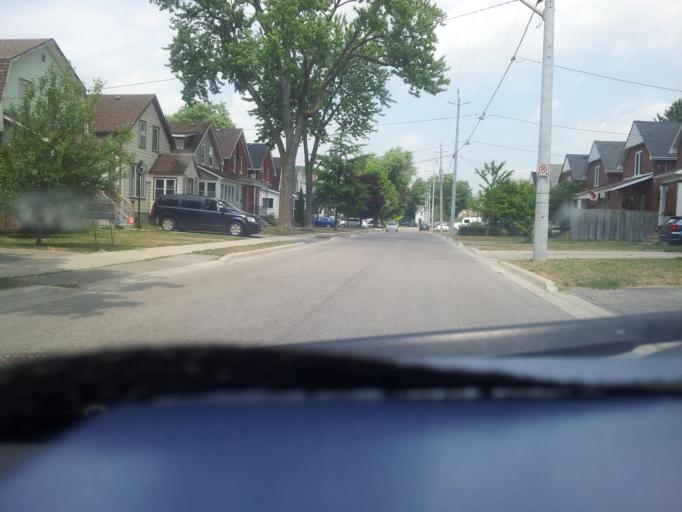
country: CA
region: Ontario
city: Stratford
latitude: 43.3674
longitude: -80.9690
